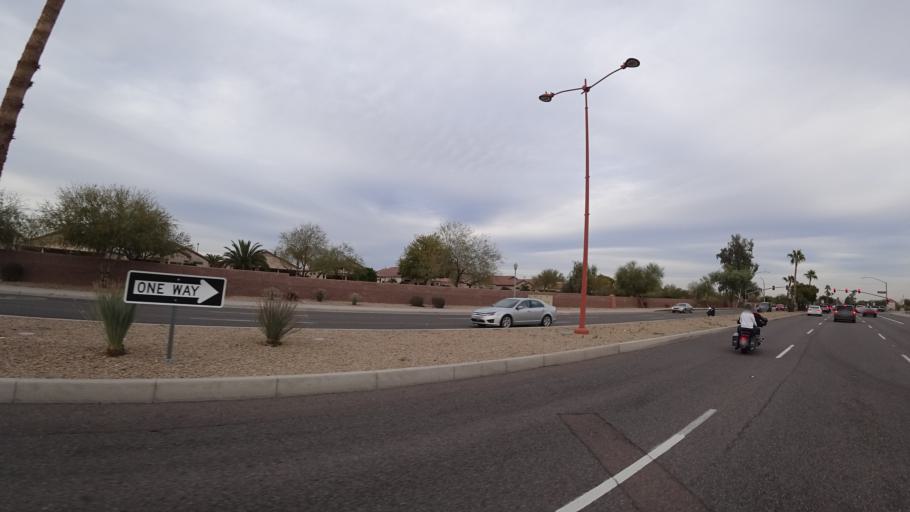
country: US
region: Arizona
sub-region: Maricopa County
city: Sun City West
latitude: 33.6387
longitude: -112.4154
